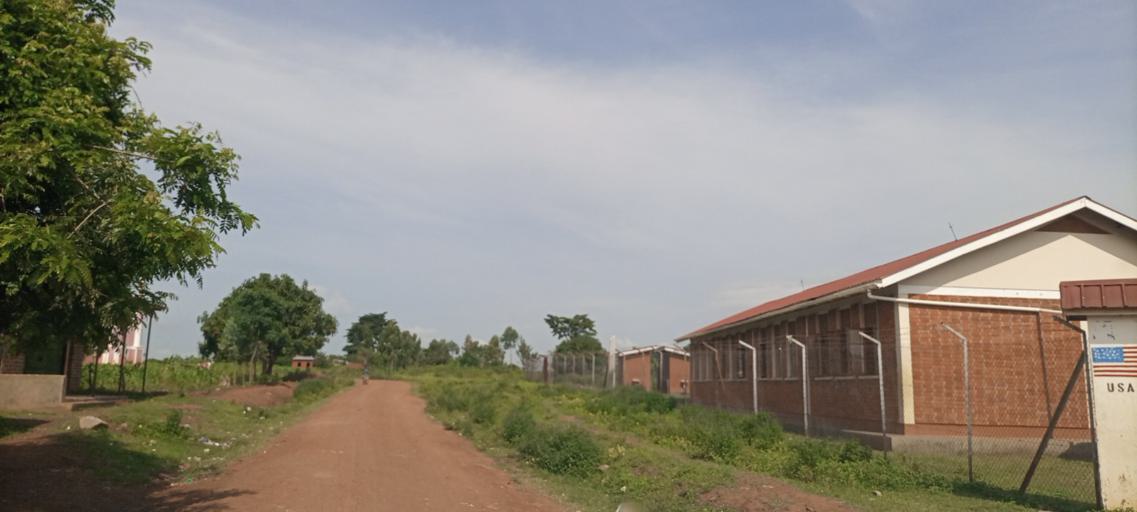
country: UG
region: Eastern Region
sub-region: Mbale District
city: Mbale
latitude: 1.1304
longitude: 34.0452
